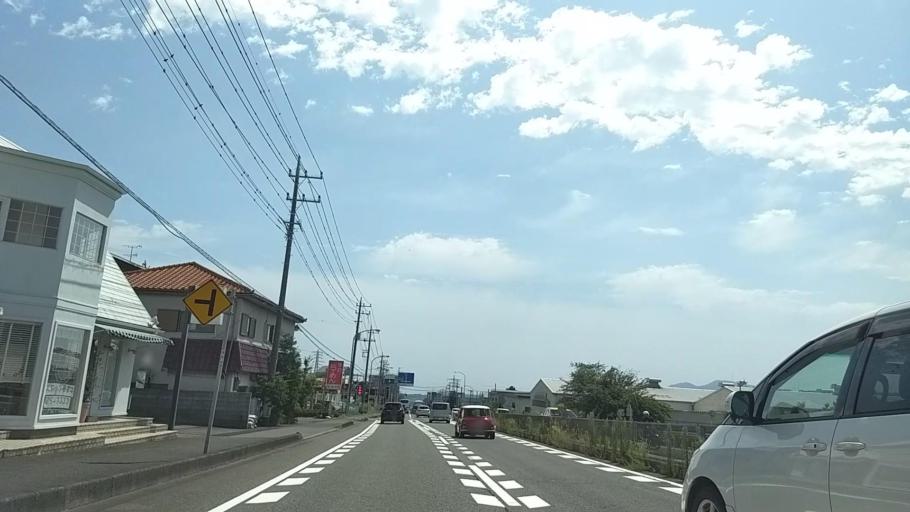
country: JP
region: Shizuoka
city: Fujinomiya
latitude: 35.2476
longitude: 138.6176
